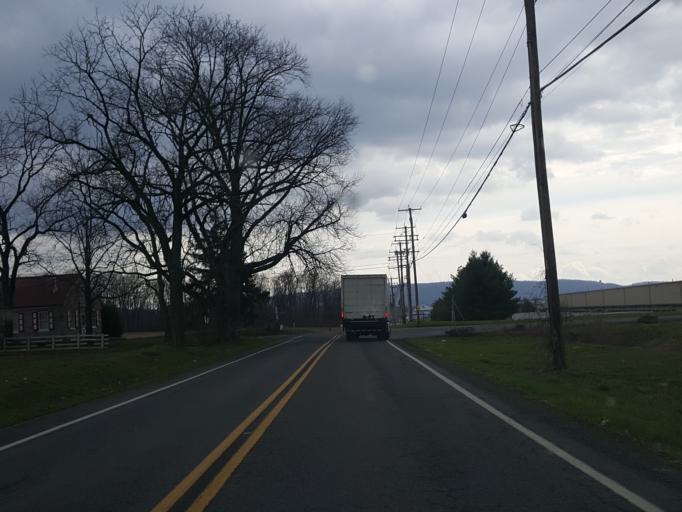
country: US
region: Pennsylvania
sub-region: Berks County
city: Fox Chase
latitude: 40.3882
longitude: -75.9785
